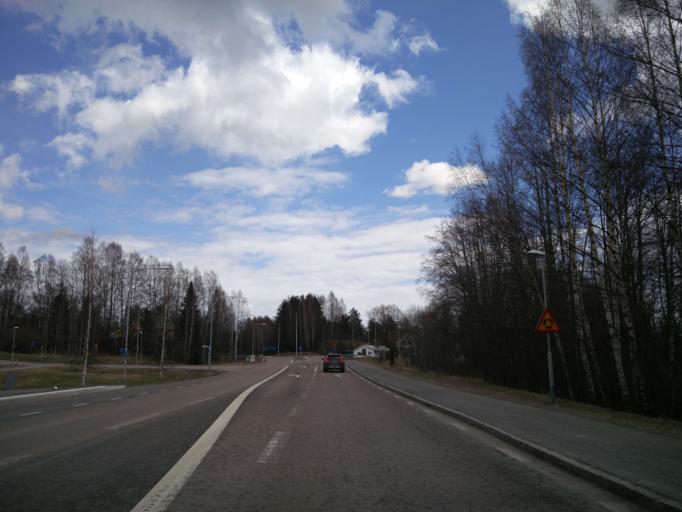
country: SE
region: Vaesternorrland
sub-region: Sundsvalls Kommun
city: Sundsvall
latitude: 62.4152
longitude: 17.2154
